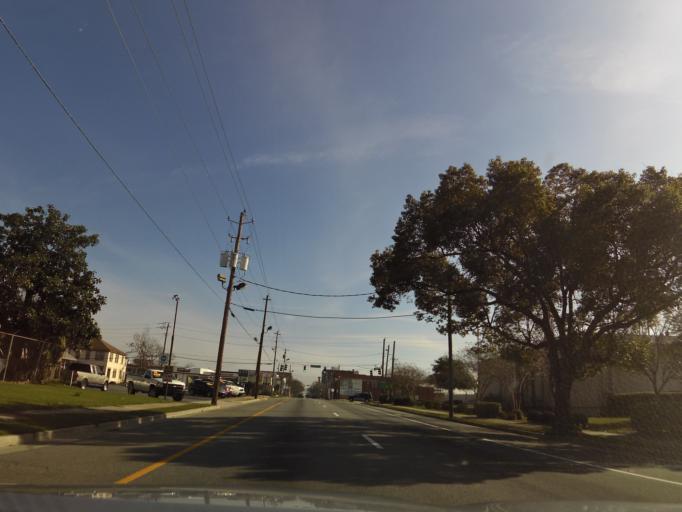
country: US
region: Georgia
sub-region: Lowndes County
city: Valdosta
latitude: 30.8294
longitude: -83.2825
